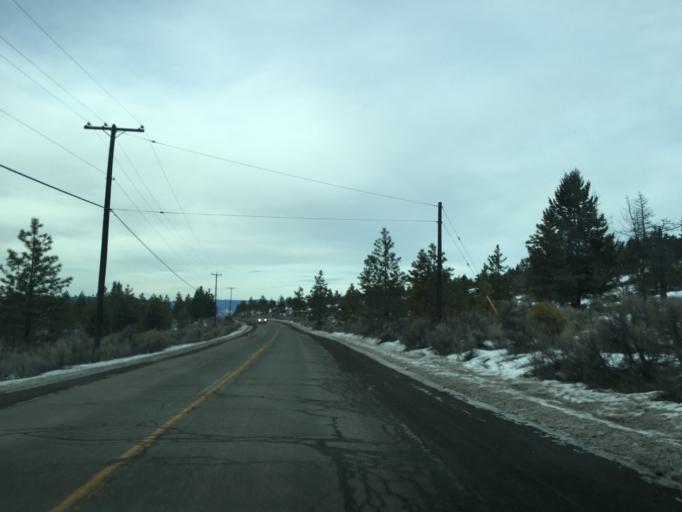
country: CA
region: British Columbia
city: Kamloops
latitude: 50.6458
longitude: -120.4507
